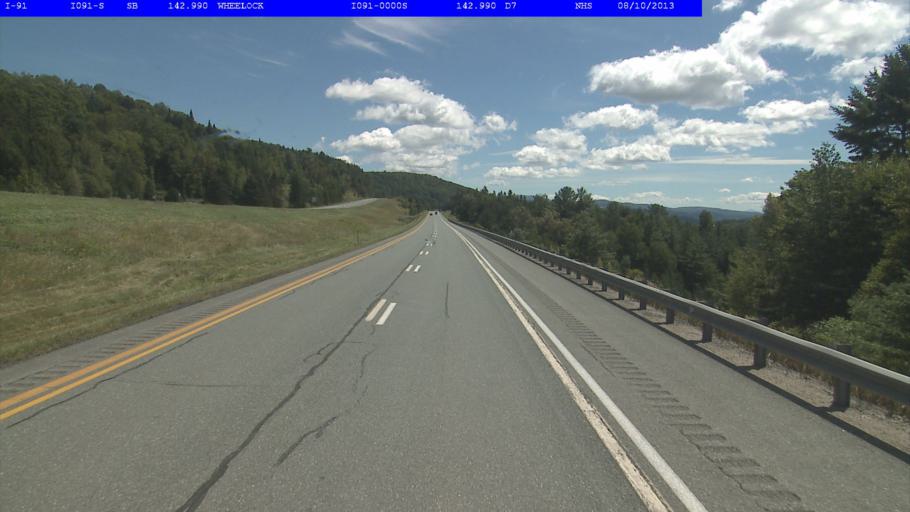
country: US
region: Vermont
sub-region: Caledonia County
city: Lyndonville
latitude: 44.5835
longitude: -72.0673
